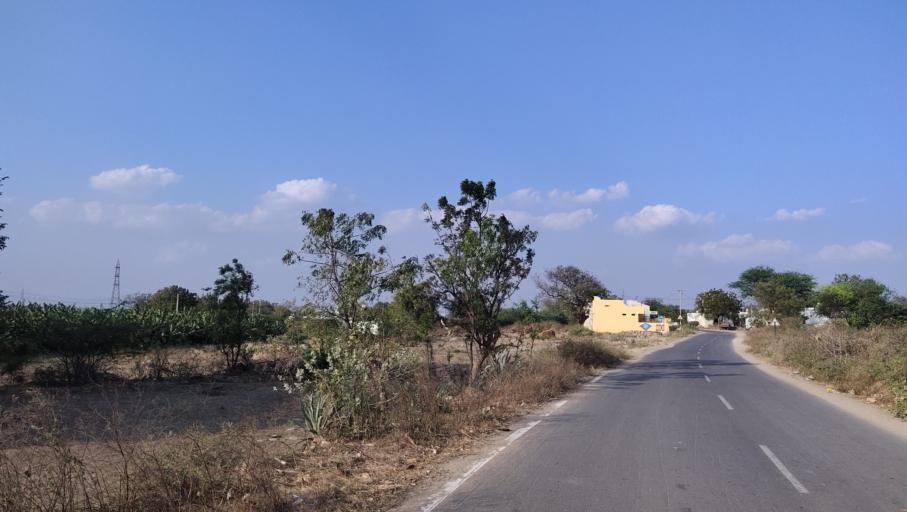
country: IN
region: Andhra Pradesh
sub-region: Anantapur
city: Tadpatri
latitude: 14.9376
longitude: 77.8660
